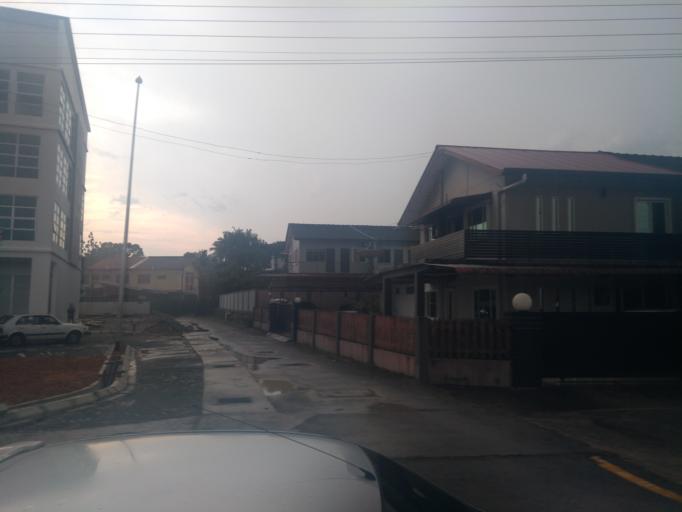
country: MY
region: Sarawak
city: Kuching
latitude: 1.5469
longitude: 110.3522
